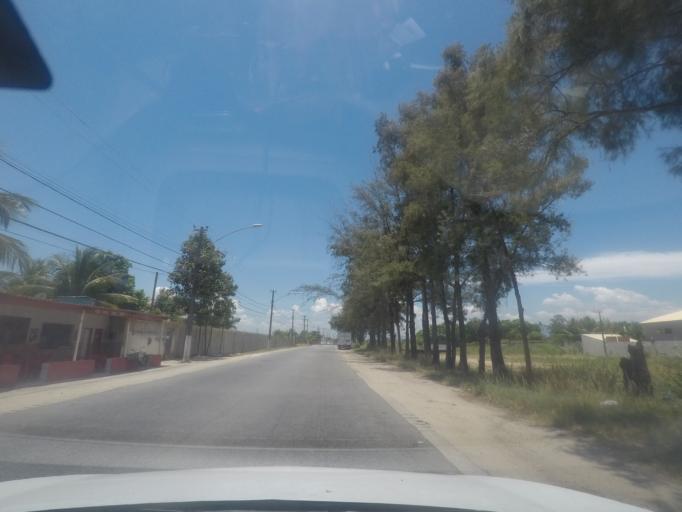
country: BR
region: Rio de Janeiro
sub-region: Itaguai
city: Itaguai
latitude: -22.9041
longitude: -43.6920
